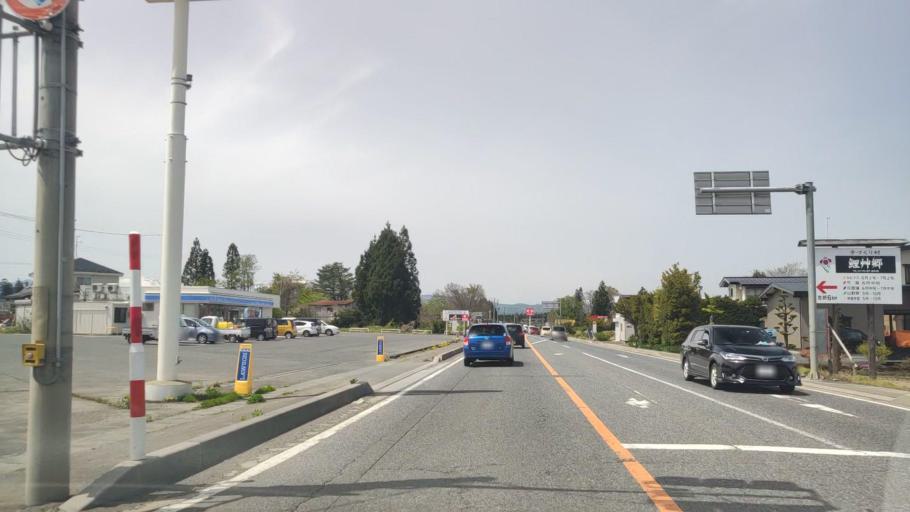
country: JP
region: Aomori
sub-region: Misawa Shi
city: Inuotose
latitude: 40.6728
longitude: 141.1809
